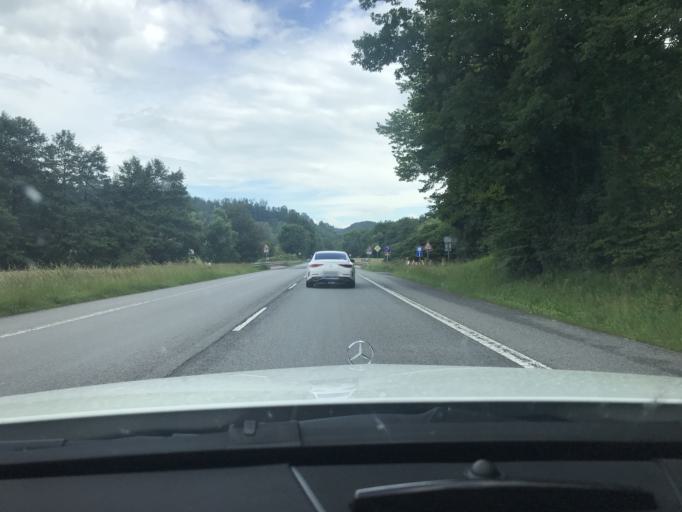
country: DE
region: Hesse
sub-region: Regierungsbezirk Kassel
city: Sontra
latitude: 51.0852
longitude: 9.9424
